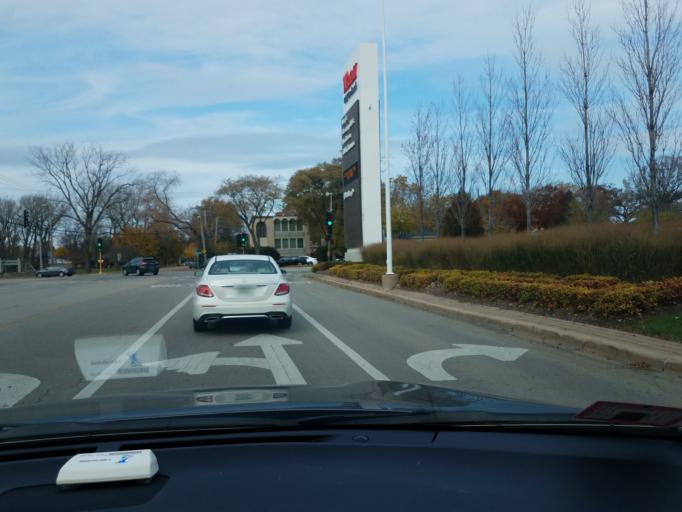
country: US
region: Illinois
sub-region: Cook County
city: Wilmette
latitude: 42.0620
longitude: -87.7514
